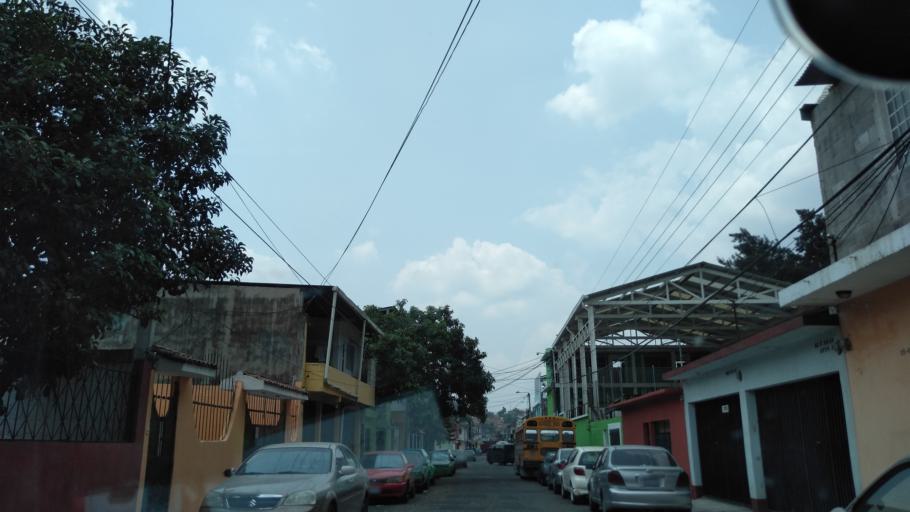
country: GT
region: Guatemala
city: Petapa
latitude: 14.5233
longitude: -90.5429
